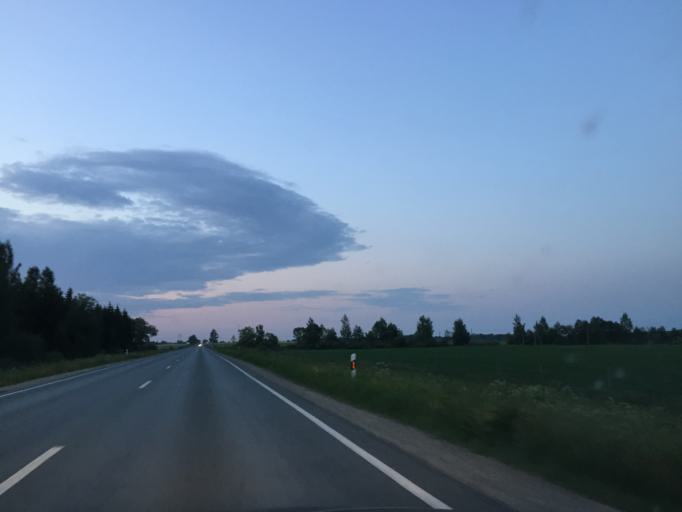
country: LT
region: Siauliu apskritis
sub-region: Joniskis
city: Joniskis
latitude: 56.1194
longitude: 23.4977
